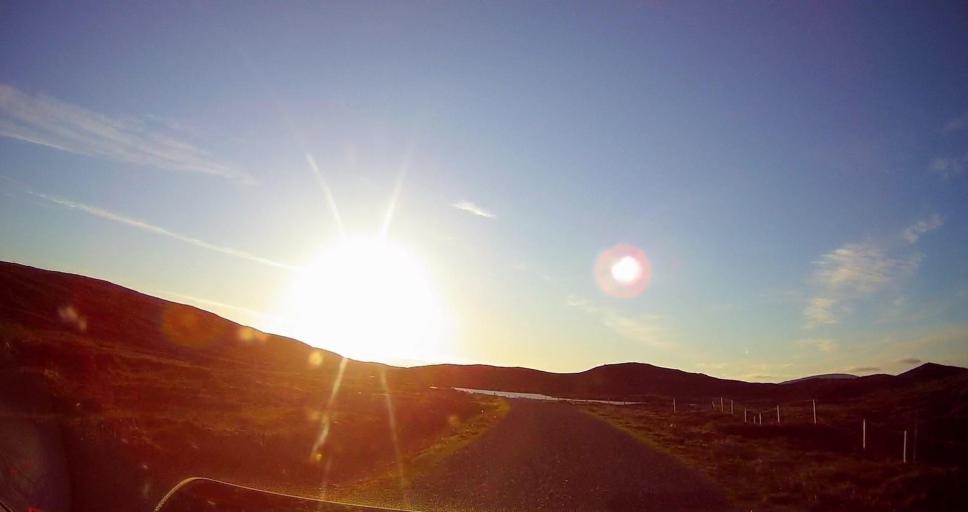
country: GB
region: Scotland
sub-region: Shetland Islands
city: Lerwick
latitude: 60.4419
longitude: -1.4030
